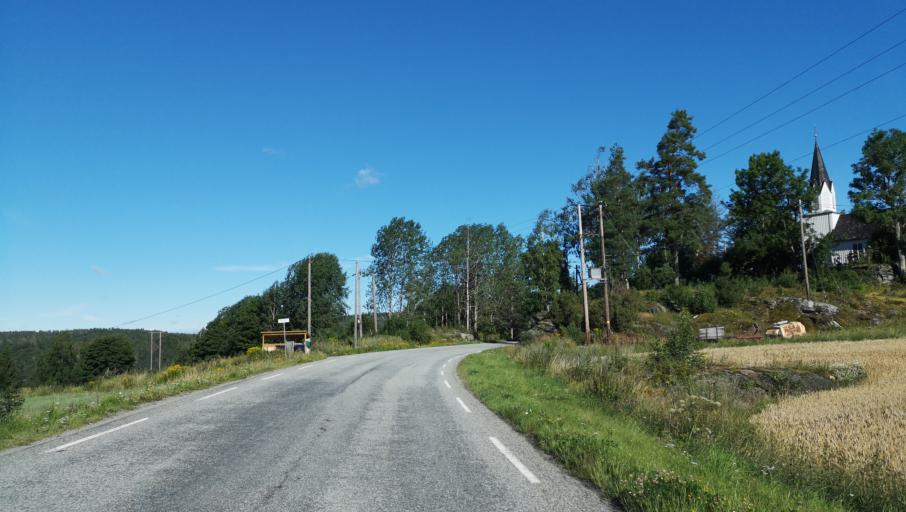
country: NO
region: Ostfold
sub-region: Hobol
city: Tomter
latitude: 59.6503
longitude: 11.0114
